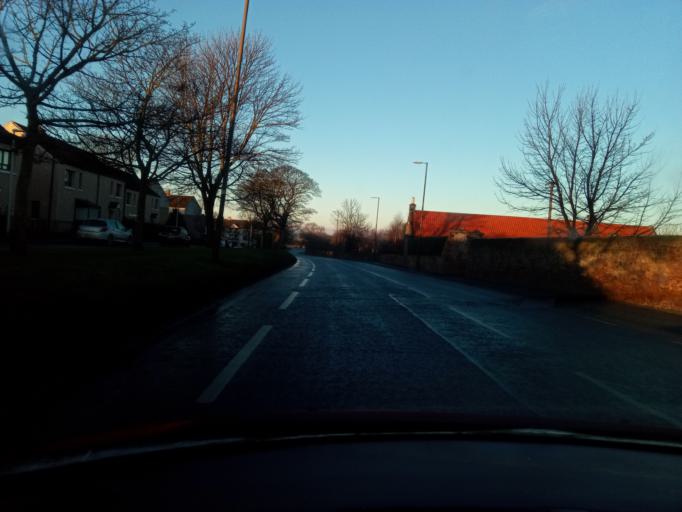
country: GB
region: Scotland
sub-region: East Lothian
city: Musselburgh
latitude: 55.9433
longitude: -3.0175
